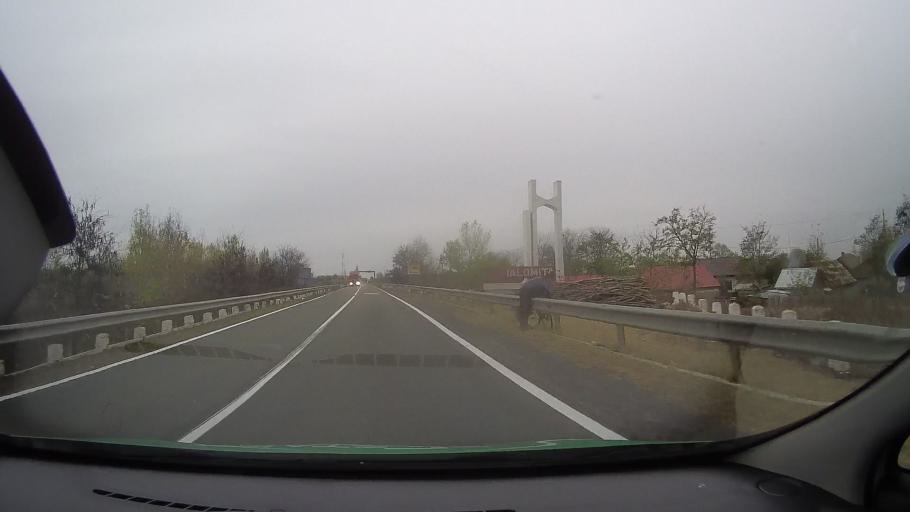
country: RO
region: Ialomita
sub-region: Comuna Giurgeni
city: Giurgeni
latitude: 44.7523
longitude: 27.8575
